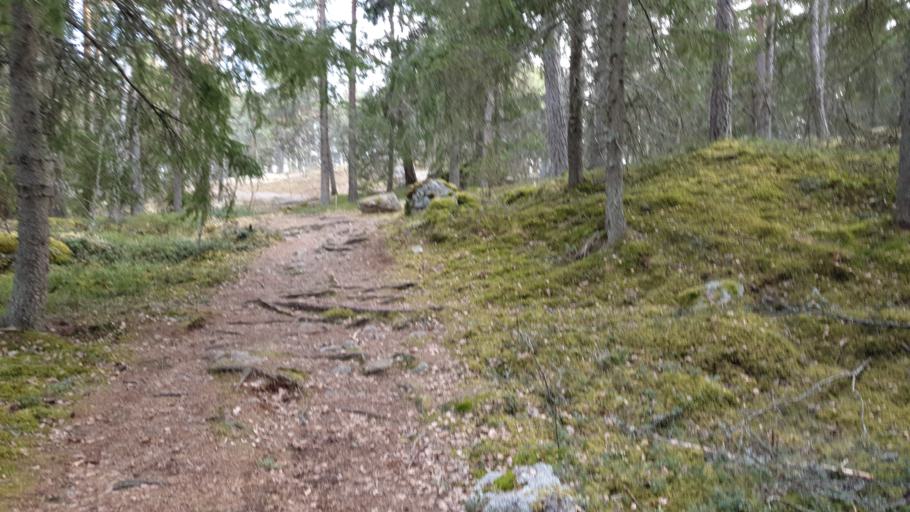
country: SE
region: Uppsala
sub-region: Enkopings Kommun
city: Grillby
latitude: 59.5993
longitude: 17.1617
